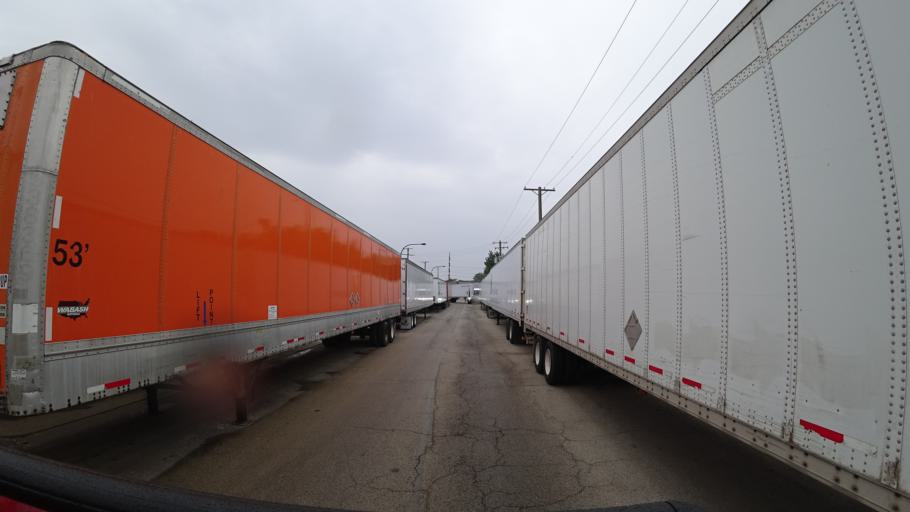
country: US
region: Illinois
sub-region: Cook County
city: Cicero
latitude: 41.8623
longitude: -87.7421
